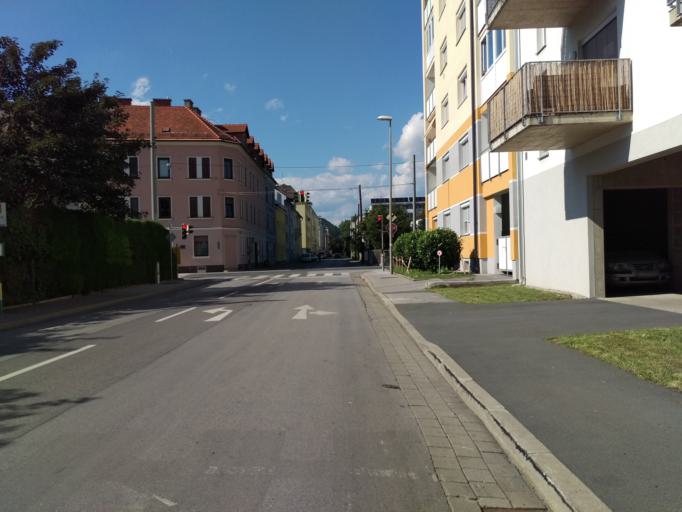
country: AT
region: Styria
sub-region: Graz Stadt
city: Wetzelsdorf
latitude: 47.0633
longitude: 15.4032
